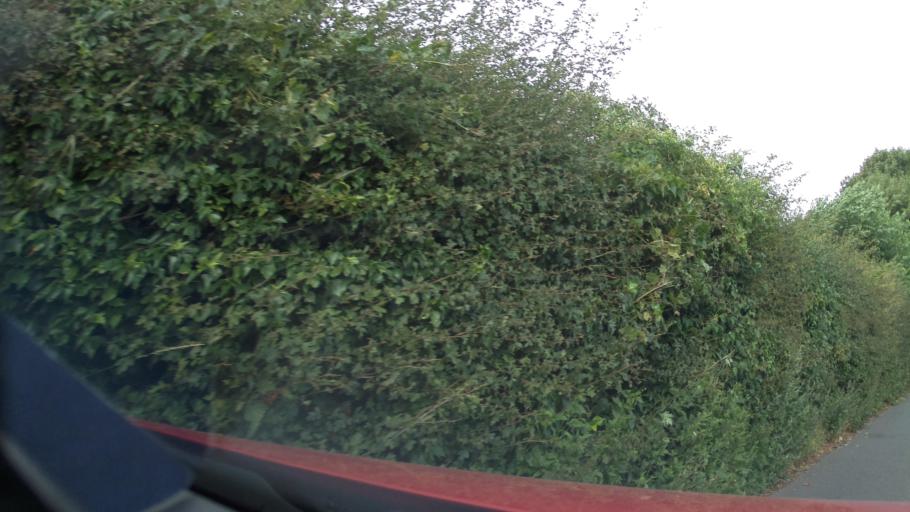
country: GB
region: England
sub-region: Derbyshire
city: Ilkeston
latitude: 52.9305
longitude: -1.3072
